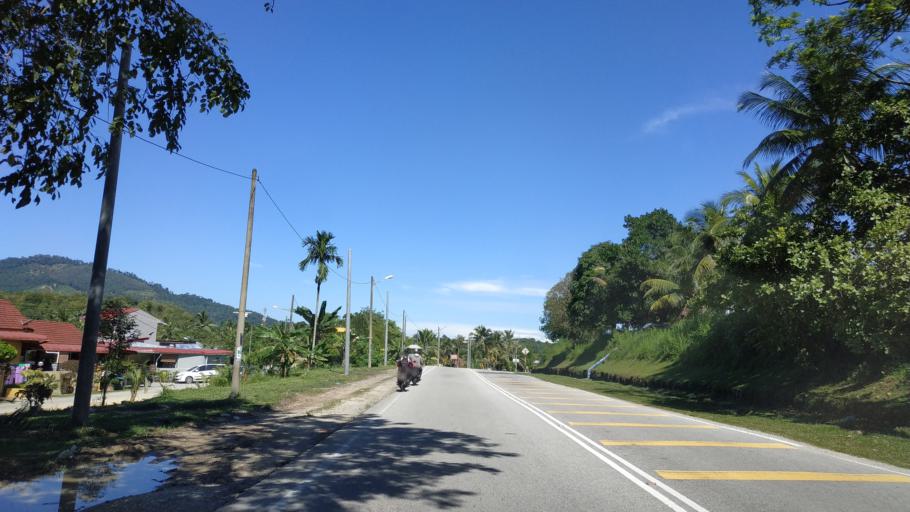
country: MY
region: Kedah
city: Kulim
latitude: 5.3454
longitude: 100.5380
